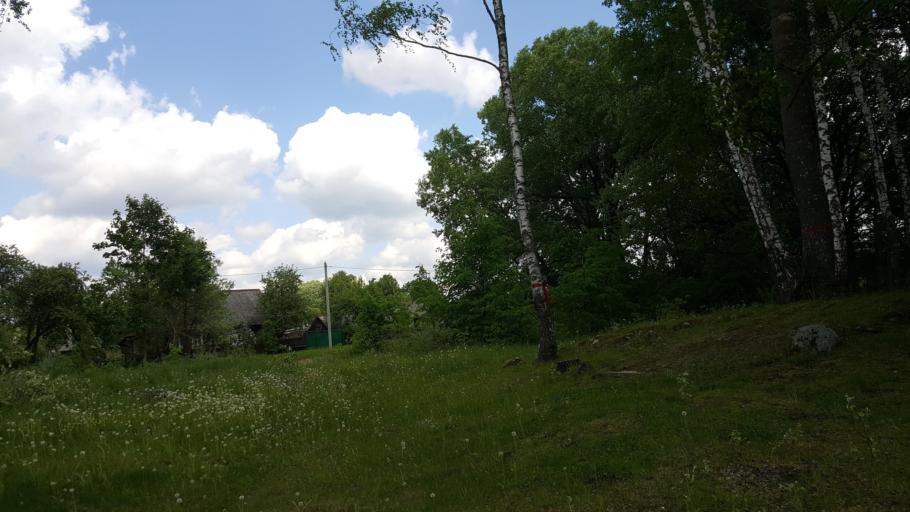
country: BY
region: Brest
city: Kamyanyets
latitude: 52.4780
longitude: 23.9693
